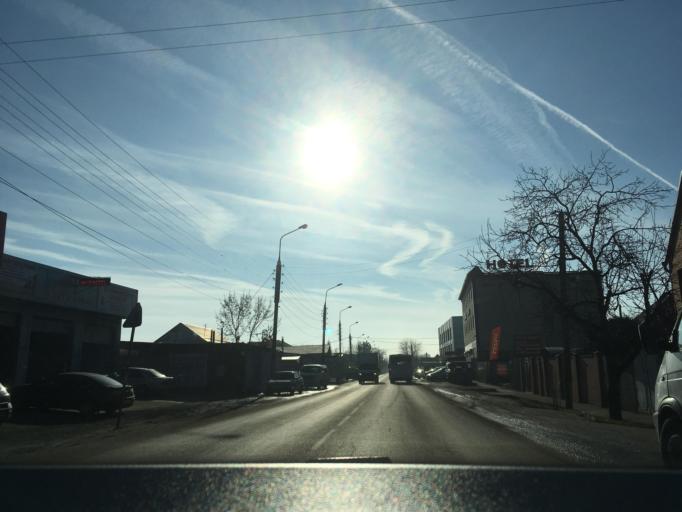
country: RU
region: Krasnodarskiy
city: Krasnodar
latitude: 45.1251
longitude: 39.0110
